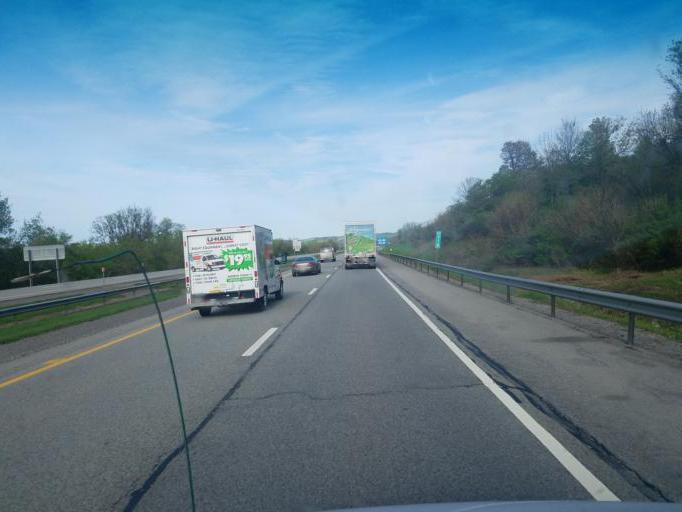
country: US
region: New York
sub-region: Herkimer County
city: Herkimer
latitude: 43.0145
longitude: -74.9576
